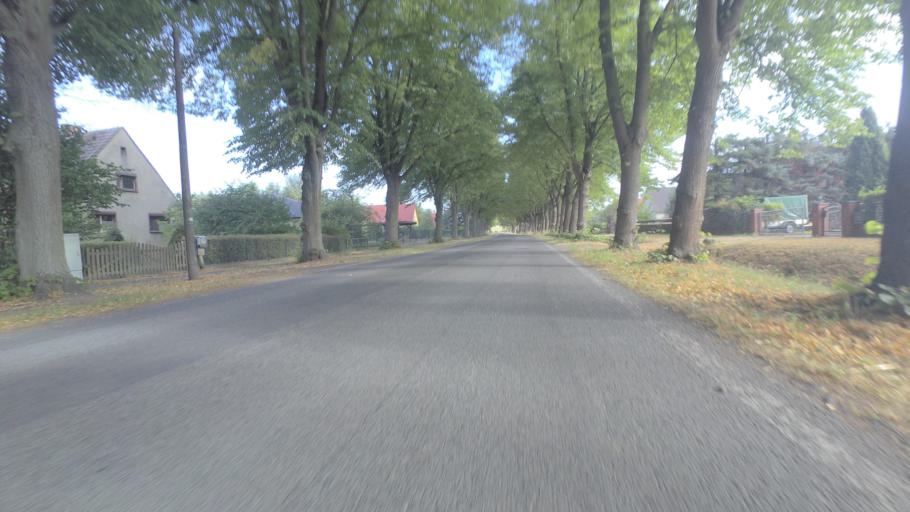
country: DE
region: Brandenburg
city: Kremmen
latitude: 52.7376
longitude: 12.9540
